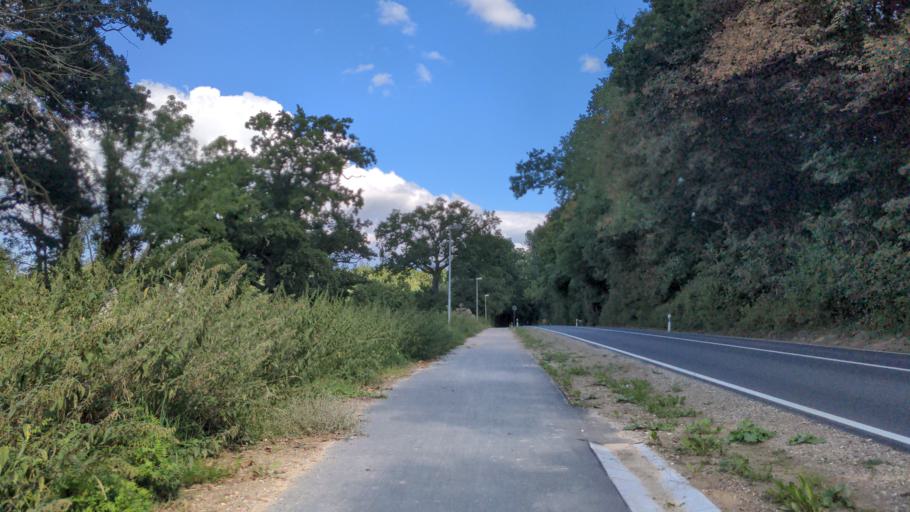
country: DE
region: Schleswig-Holstein
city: Lensahn
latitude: 54.2127
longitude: 10.8626
